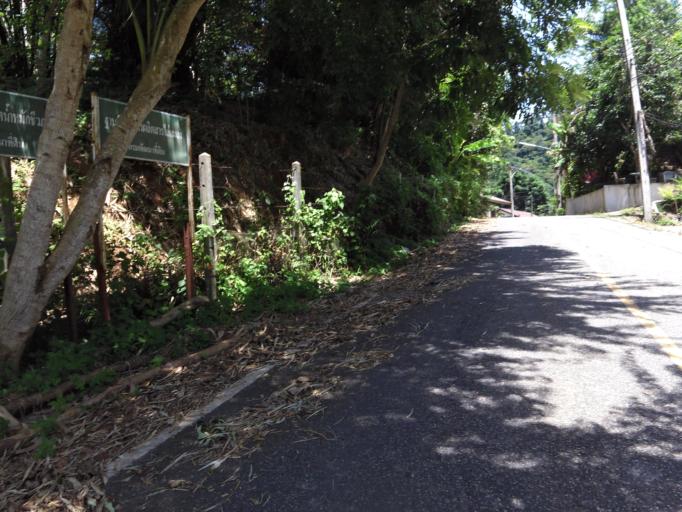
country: TH
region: Phuket
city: Ban Karon
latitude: 7.8482
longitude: 98.3078
